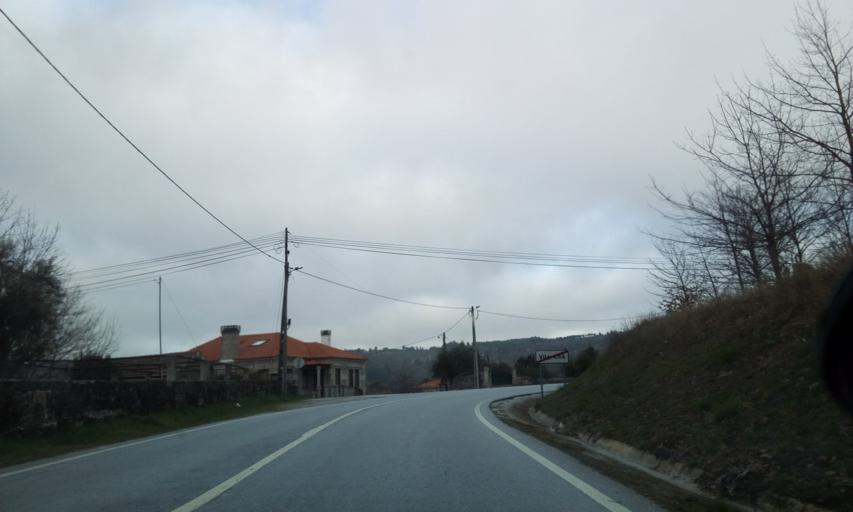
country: PT
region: Guarda
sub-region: Fornos de Algodres
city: Fornos de Algodres
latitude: 40.6566
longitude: -7.4840
